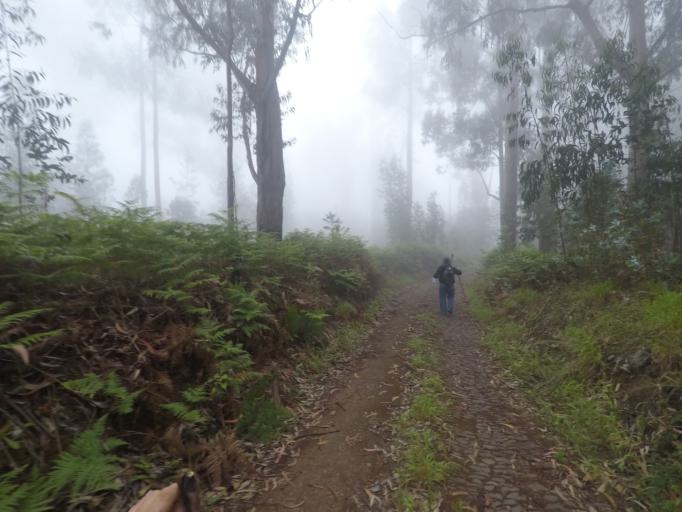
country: PT
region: Madeira
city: Ponta do Sol
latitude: 32.7196
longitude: -17.0924
